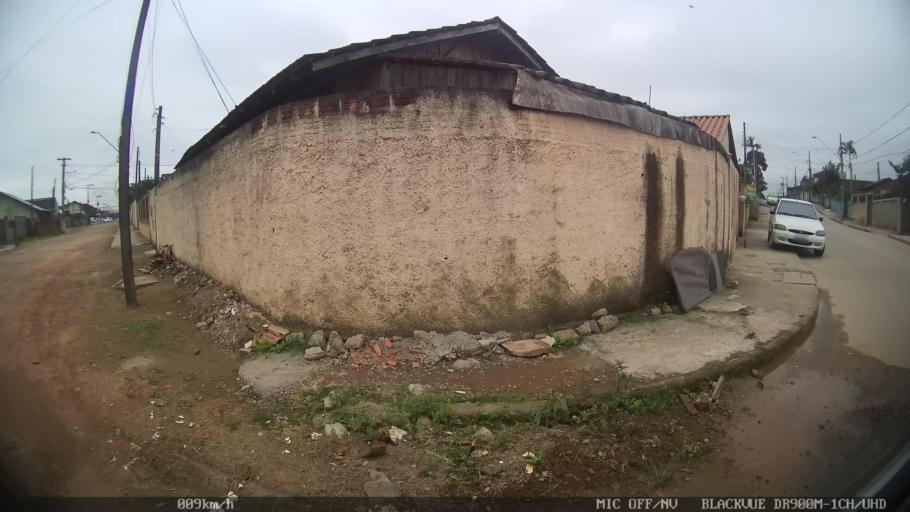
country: BR
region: Santa Catarina
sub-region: Joinville
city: Joinville
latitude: -26.3214
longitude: -48.8188
